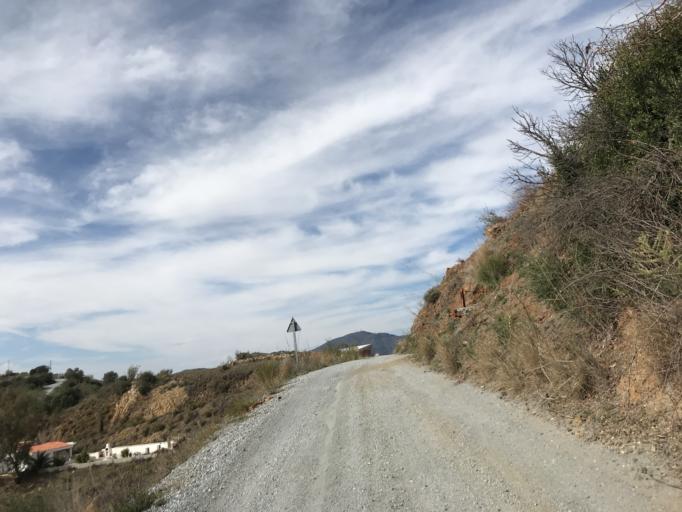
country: ES
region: Andalusia
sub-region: Provincia de Malaga
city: Almachar
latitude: 36.7823
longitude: -4.2201
